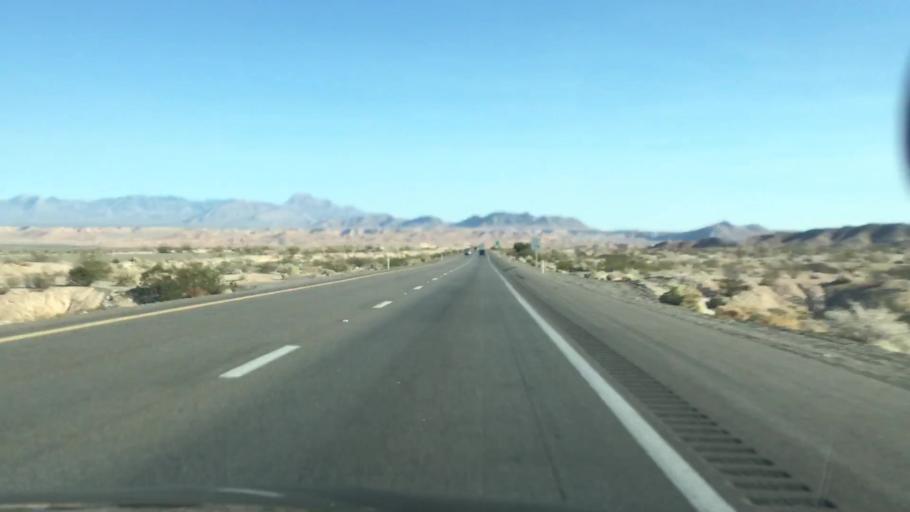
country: US
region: Nevada
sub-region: Clark County
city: Moapa Town
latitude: 36.6427
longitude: -114.5926
